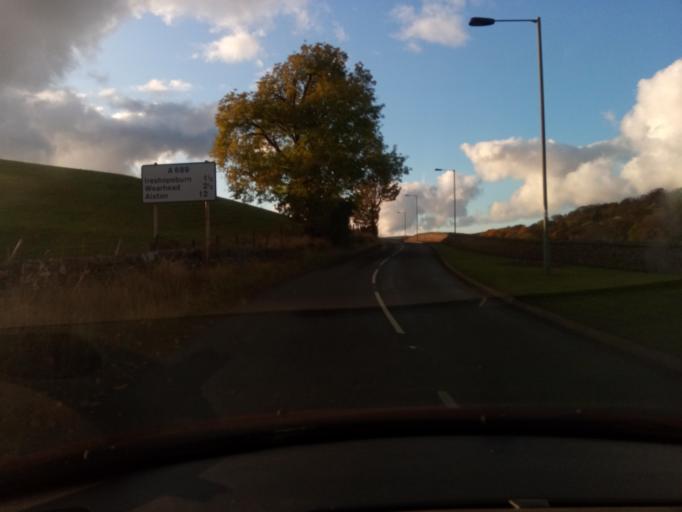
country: GB
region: England
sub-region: County Durham
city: Newbiggin
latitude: 54.7396
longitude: -2.1899
